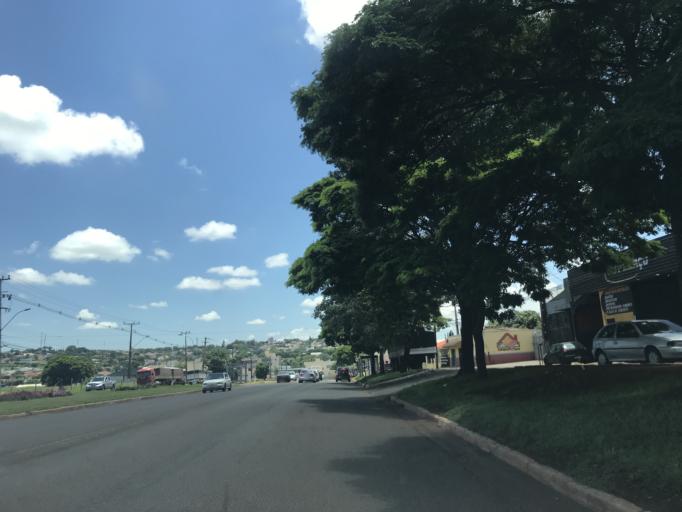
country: BR
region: Parana
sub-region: Marialva
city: Marialva
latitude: -23.4787
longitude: -51.8065
